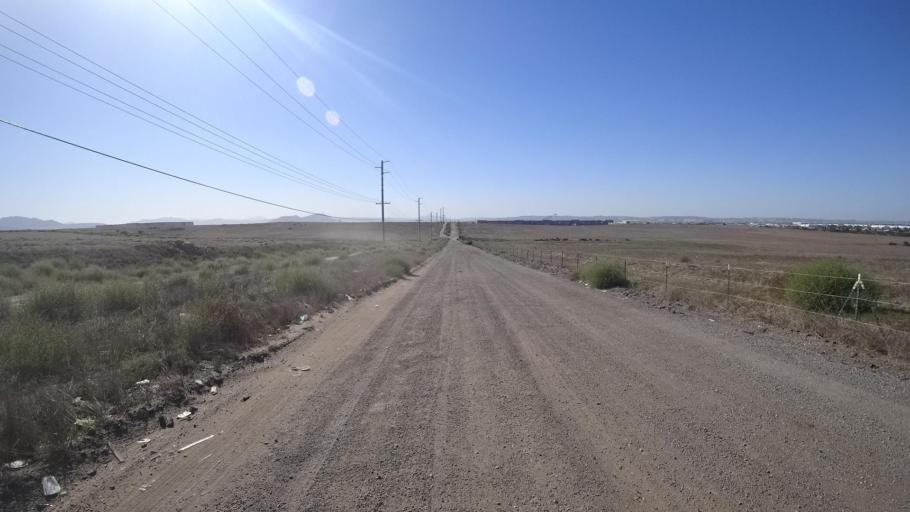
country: MX
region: Baja California
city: Tijuana
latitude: 32.5772
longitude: -116.9452
